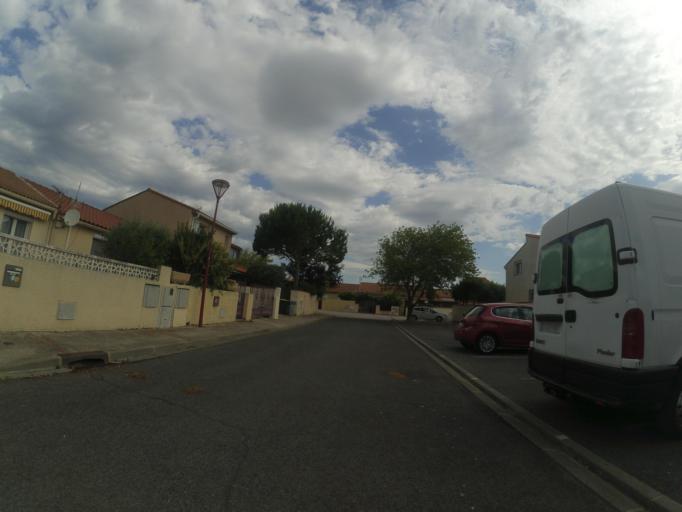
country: FR
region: Languedoc-Roussillon
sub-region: Departement des Pyrenees-Orientales
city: Toulouges
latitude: 42.6740
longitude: 2.8289
